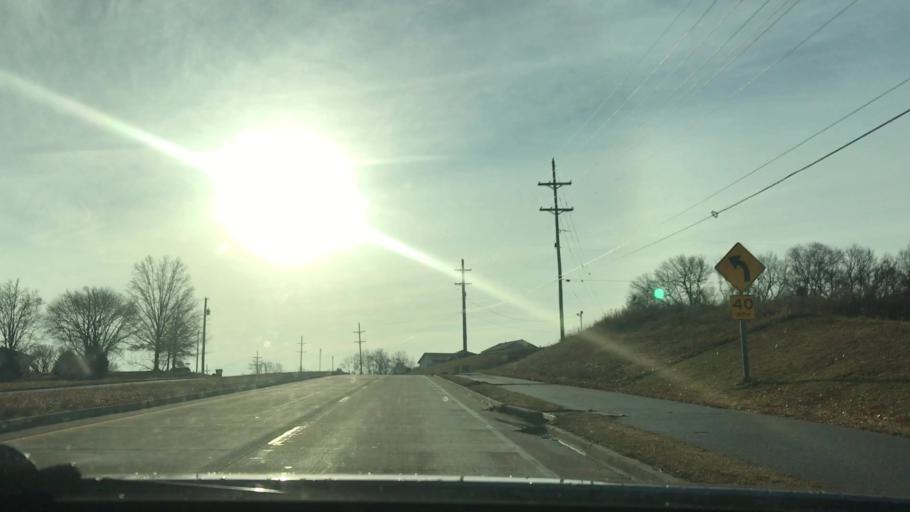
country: US
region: Missouri
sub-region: Platte County
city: Weatherby Lake
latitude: 39.2140
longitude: -94.7277
